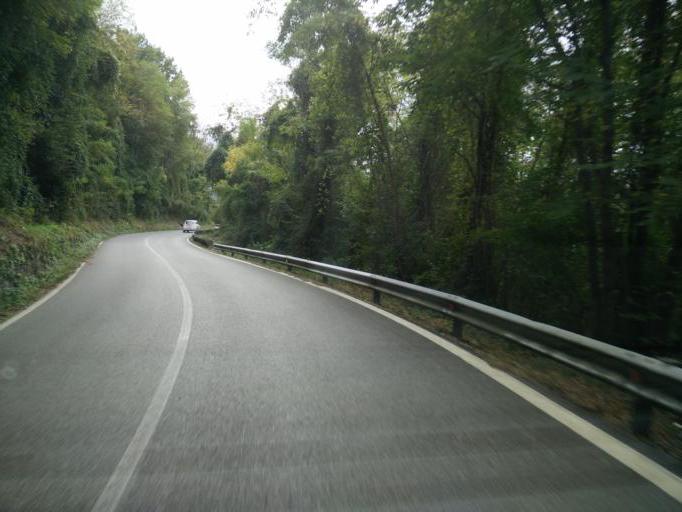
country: IT
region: Tuscany
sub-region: Provincia di Massa-Carrara
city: Fivizzano
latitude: 44.2189
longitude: 10.0953
